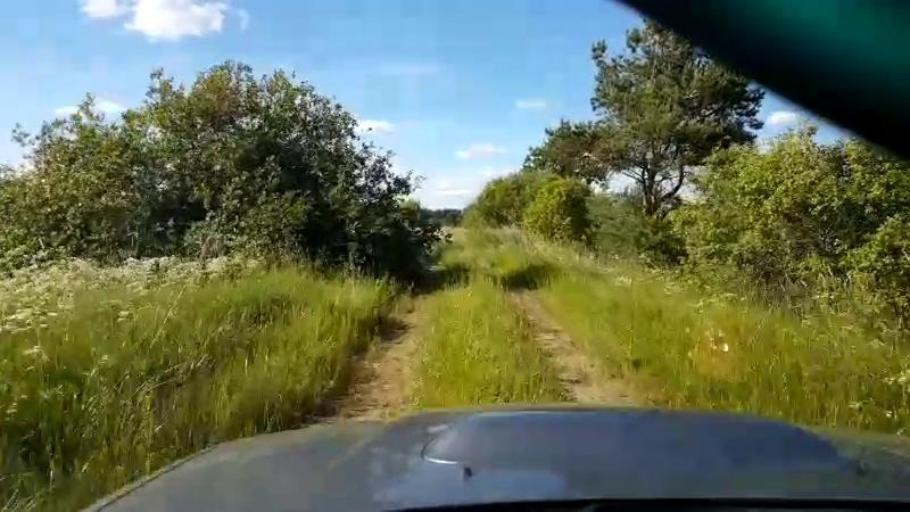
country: EE
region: Paernumaa
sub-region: Sauga vald
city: Sauga
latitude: 58.5042
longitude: 24.5906
